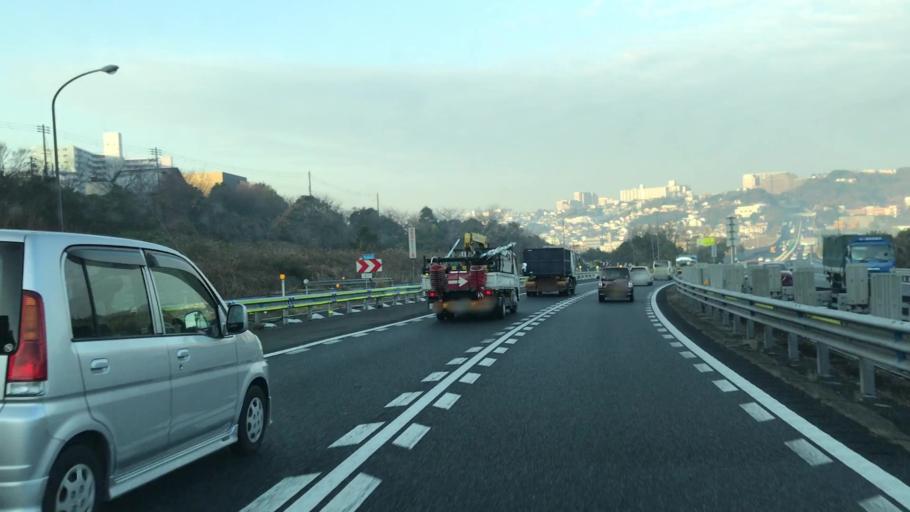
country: JP
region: Hyogo
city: Akashi
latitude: 34.6476
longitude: 135.0752
